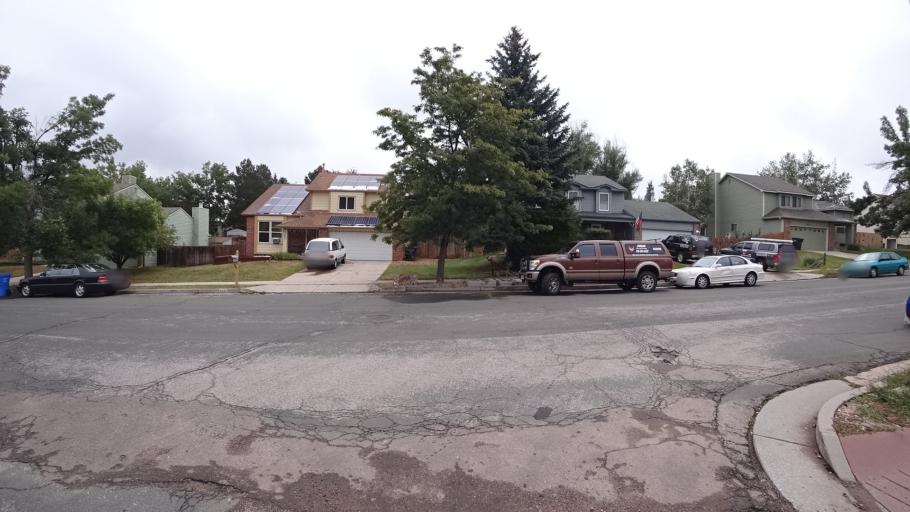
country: US
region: Colorado
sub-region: El Paso County
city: Cimarron Hills
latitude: 38.9256
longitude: -104.7606
